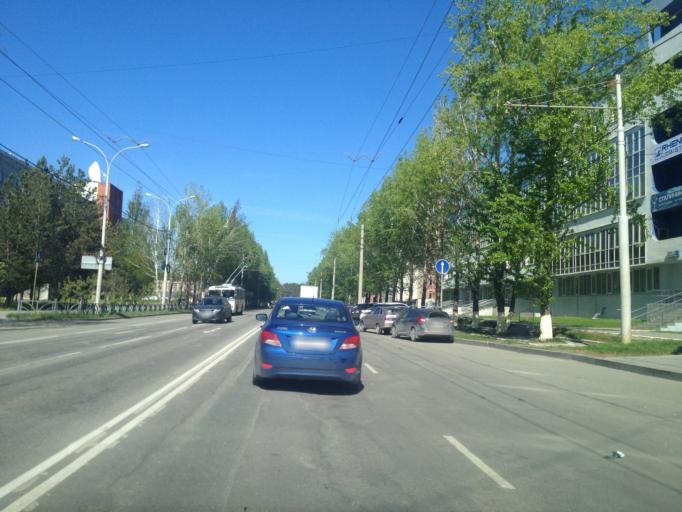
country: RU
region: Sverdlovsk
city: Sovkhoznyy
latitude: 56.7765
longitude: 60.5526
